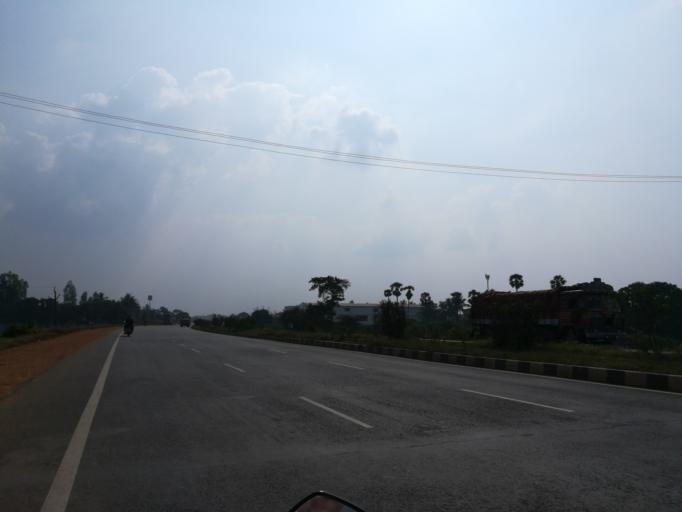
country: IN
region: Andhra Pradesh
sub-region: Nellore
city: Kovur
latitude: 14.5354
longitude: 79.9917
